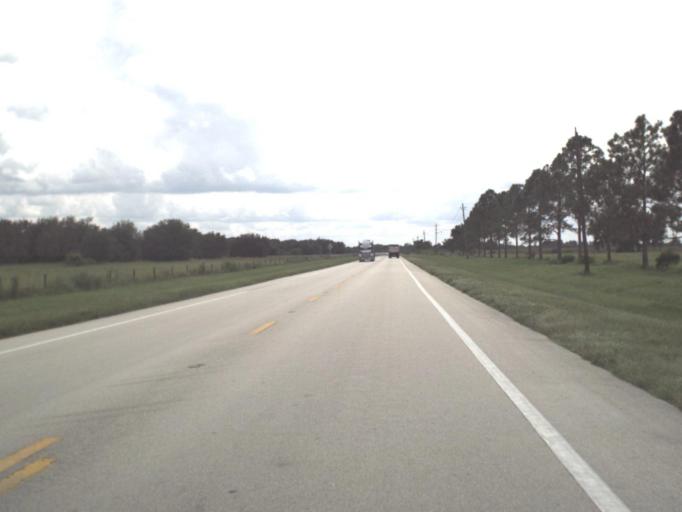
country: US
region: Florida
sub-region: DeSoto County
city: Southeast Arcadia
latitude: 27.1356
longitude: -81.7962
